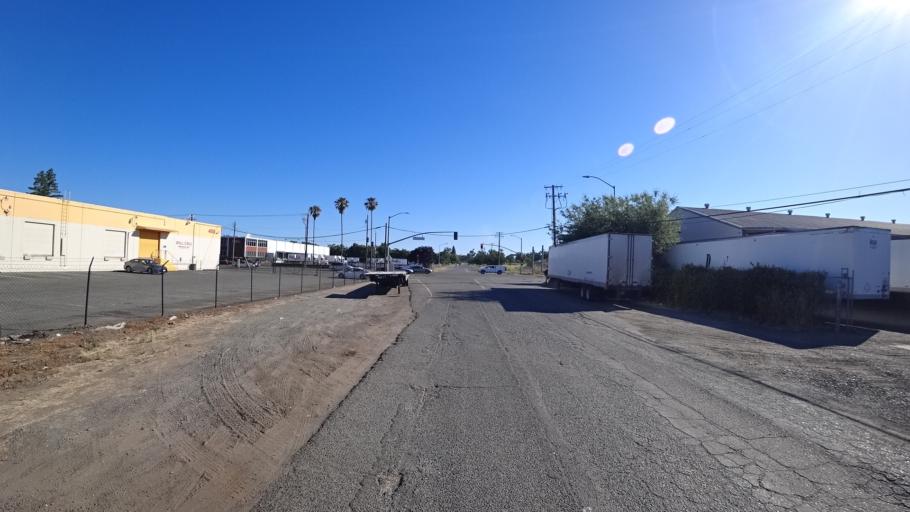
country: US
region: California
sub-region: Sacramento County
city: Sacramento
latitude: 38.5962
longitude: -121.4952
